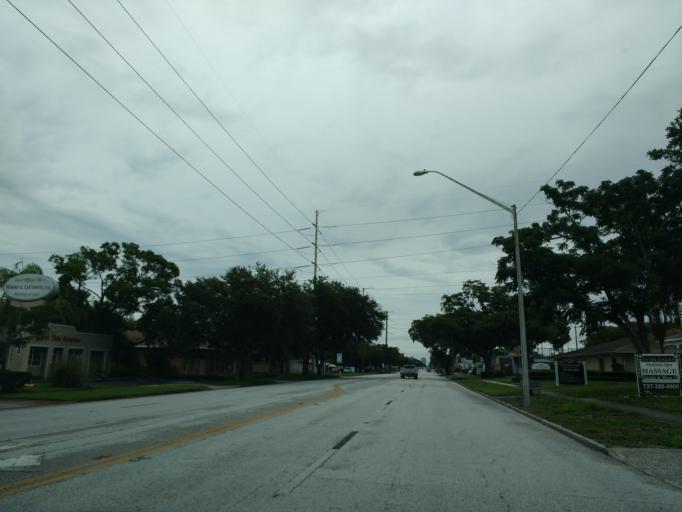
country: US
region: Florida
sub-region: Pinellas County
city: Gulfport
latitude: 27.7709
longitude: -82.7049
